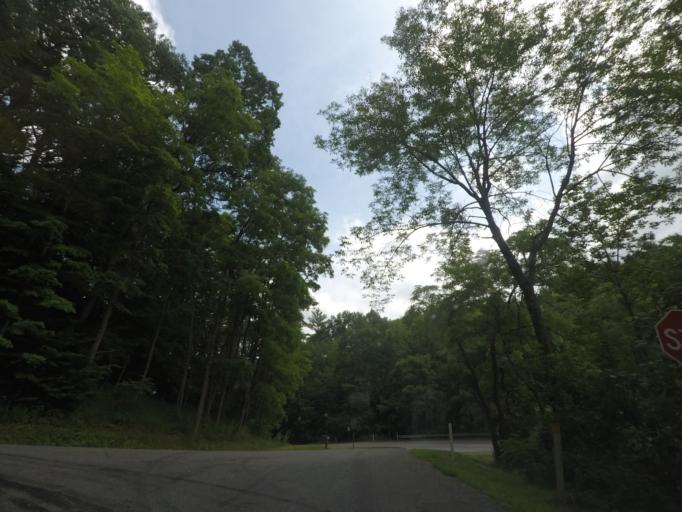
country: US
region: New York
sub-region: Saratoga County
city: Stillwater
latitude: 43.0076
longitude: -73.6190
